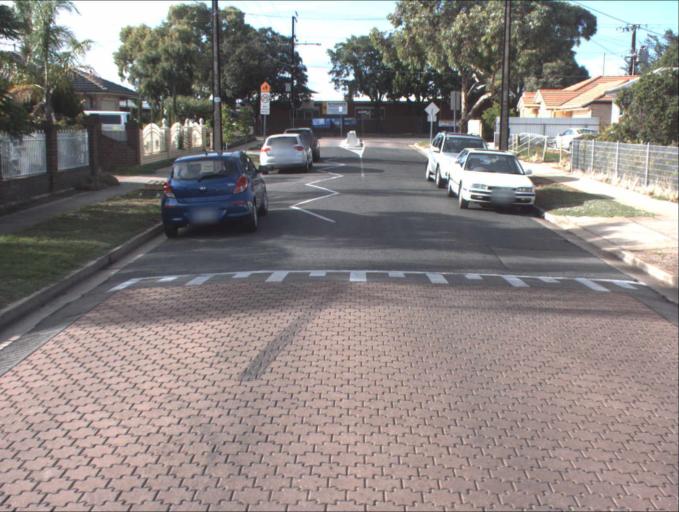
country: AU
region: South Australia
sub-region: Charles Sturt
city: Woodville North
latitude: -34.8534
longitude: 138.5514
